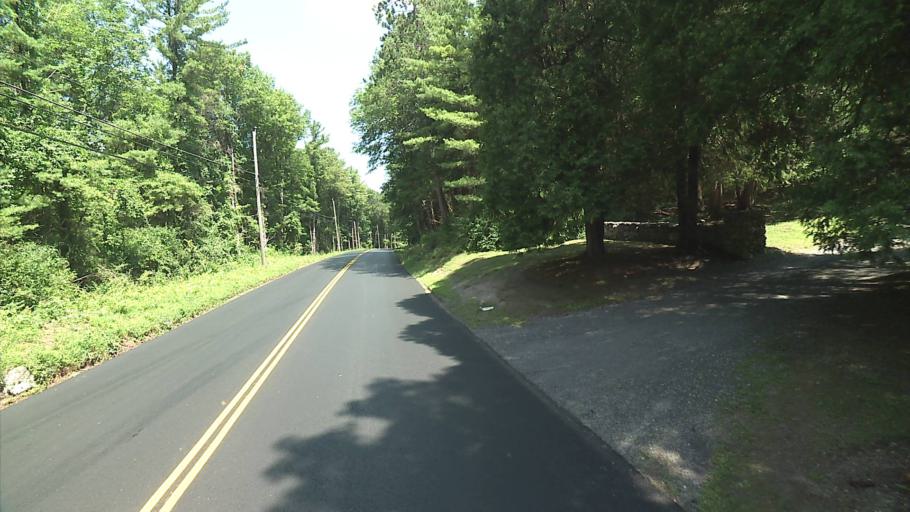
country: US
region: Connecticut
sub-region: Litchfield County
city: Canaan
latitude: 41.9972
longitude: -73.3603
